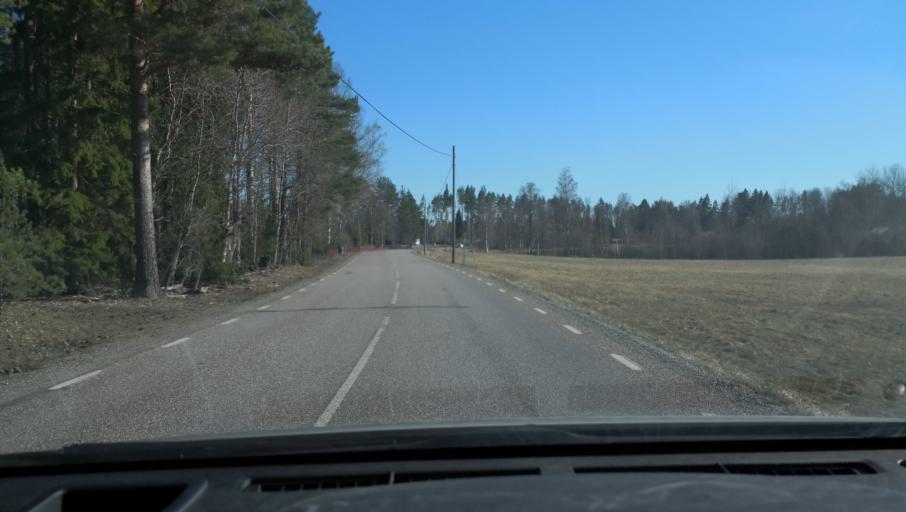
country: SE
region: Dalarna
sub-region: Avesta Kommun
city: Avesta
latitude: 60.0016
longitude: 16.3465
